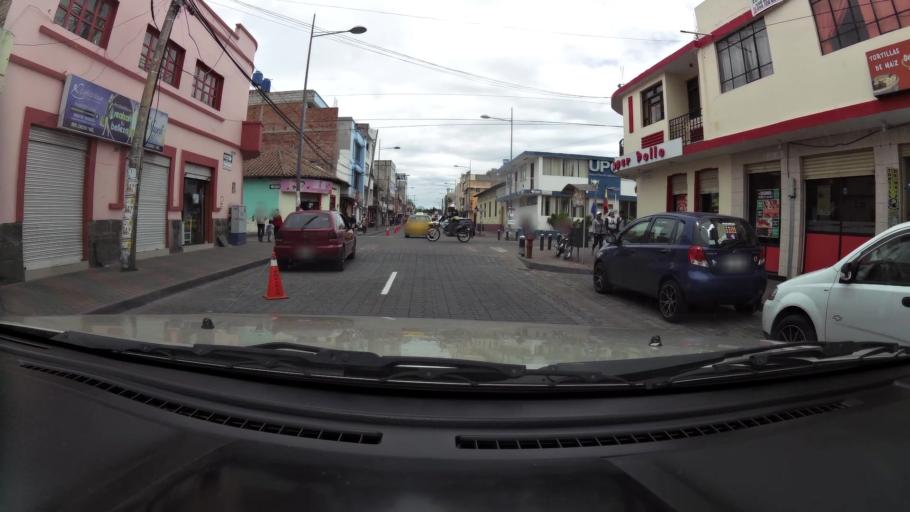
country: EC
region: Cotopaxi
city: San Miguel de Salcedo
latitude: -1.0354
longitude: -78.5873
